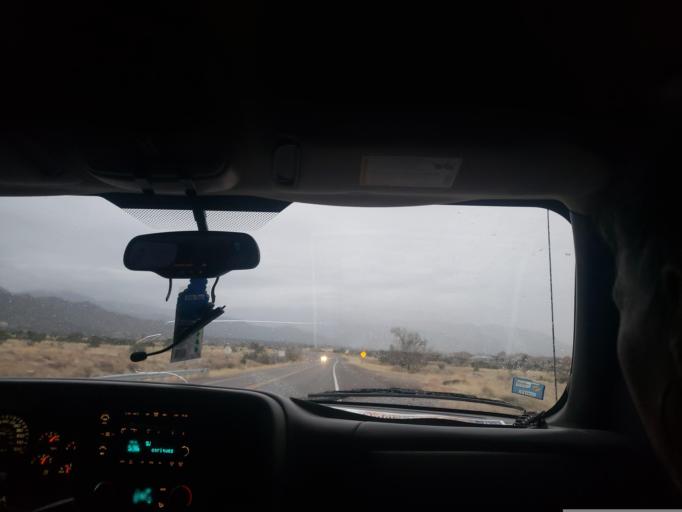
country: US
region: New Mexico
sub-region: Bernalillo County
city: Sandia Heights
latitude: 35.1990
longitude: -106.5050
